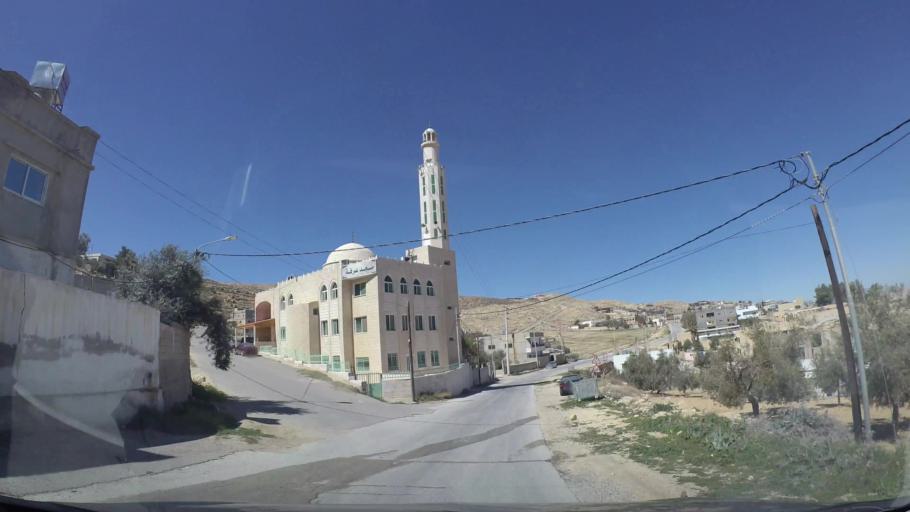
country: JO
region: Tafielah
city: At Tafilah
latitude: 30.8305
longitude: 35.5784
